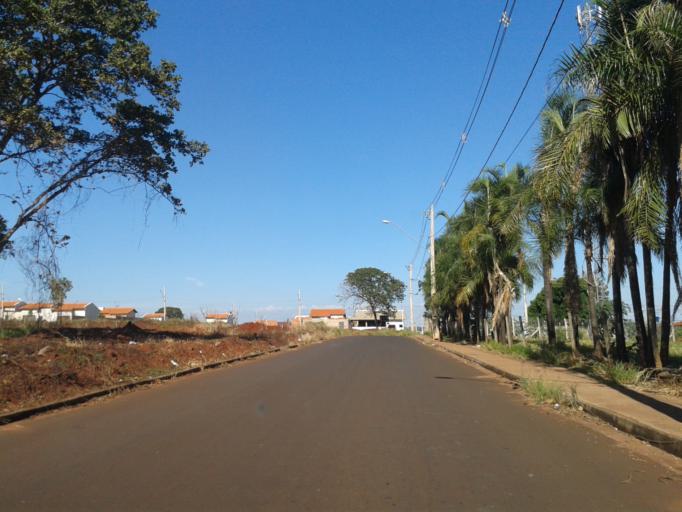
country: BR
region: Minas Gerais
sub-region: Ituiutaba
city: Ituiutaba
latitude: -18.9844
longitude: -49.4915
